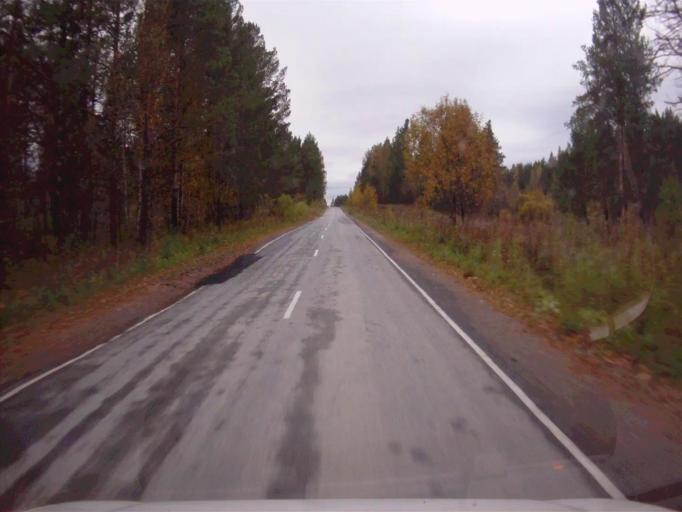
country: RU
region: Chelyabinsk
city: Nyazepetrovsk
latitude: 56.0537
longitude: 59.4796
